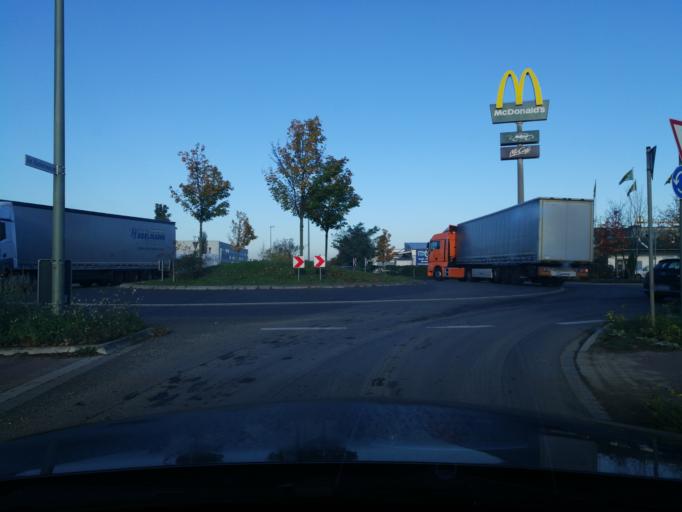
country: DE
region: North Rhine-Westphalia
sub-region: Regierungsbezirk Dusseldorf
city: Dusseldorf
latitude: 51.1628
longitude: 6.7527
